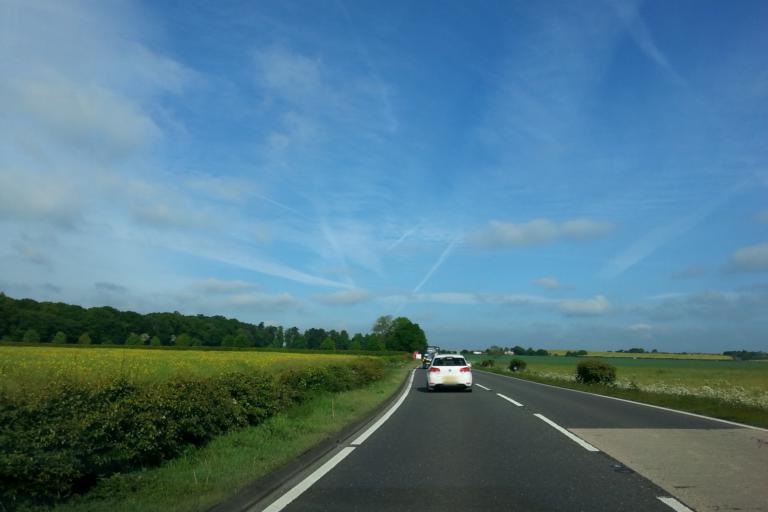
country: GB
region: England
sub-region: Nottinghamshire
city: Farnsfield
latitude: 53.1197
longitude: -1.0095
